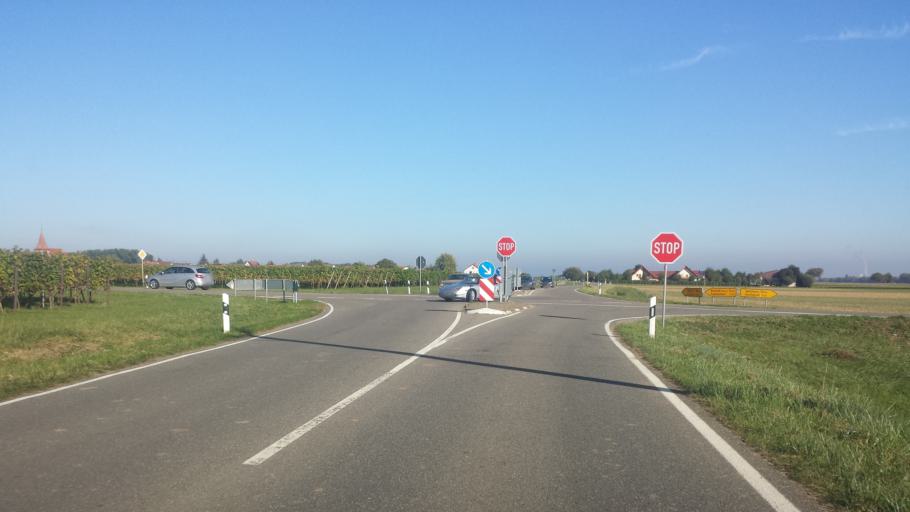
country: DE
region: Rheinland-Pfalz
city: Hochstadt
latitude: 49.2657
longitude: 8.2179
